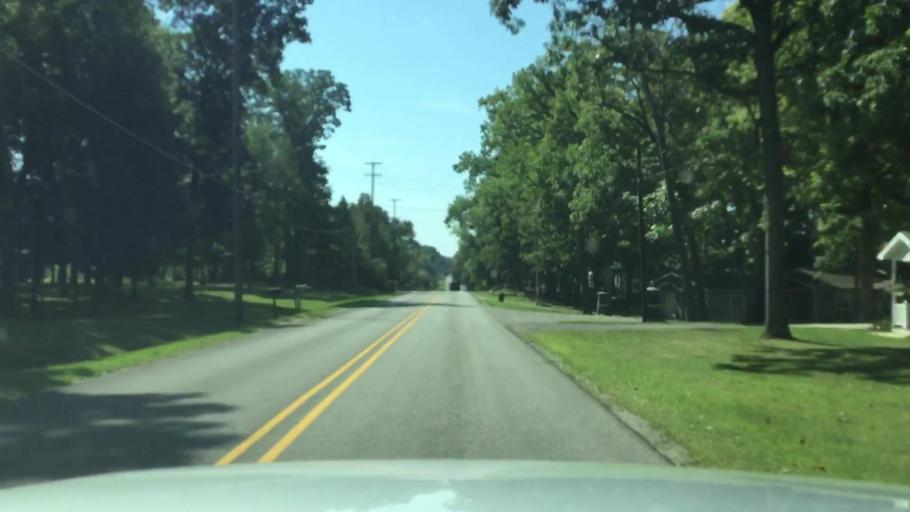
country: US
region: Michigan
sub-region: Lenawee County
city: Manitou Beach-Devils Lake
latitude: 42.0022
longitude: -84.2809
